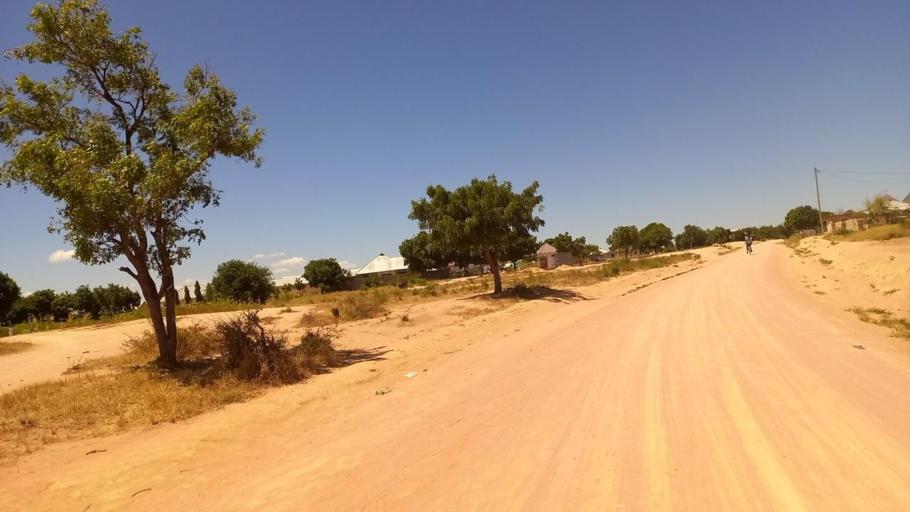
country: TZ
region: Dodoma
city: Dodoma
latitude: -6.1298
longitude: 35.7305
